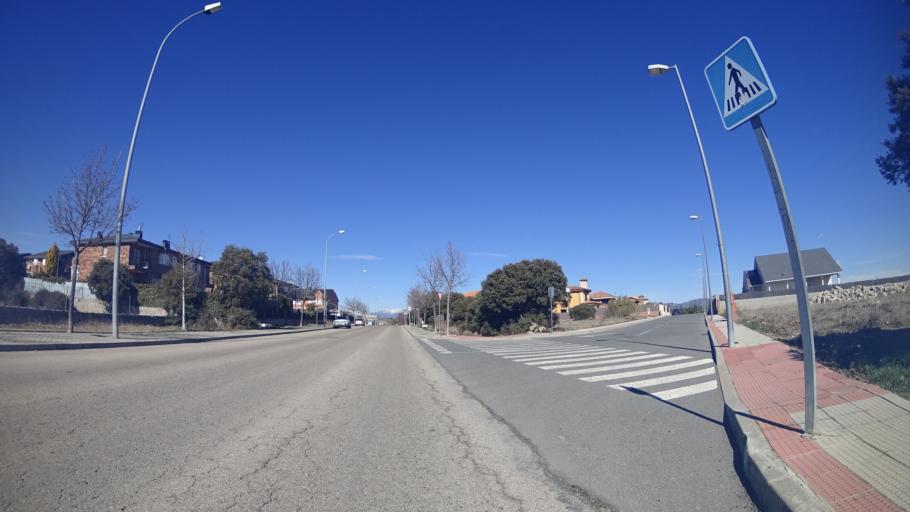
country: ES
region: Madrid
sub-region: Provincia de Madrid
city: Colmenarejo
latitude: 40.5485
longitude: -4.0112
